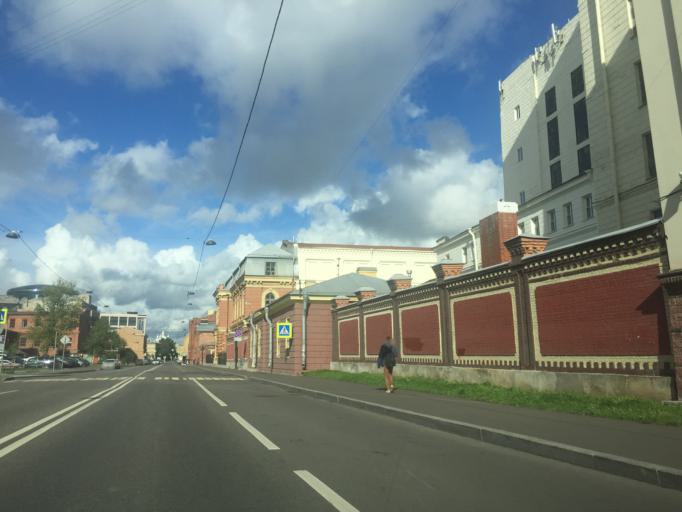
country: RU
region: St.-Petersburg
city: Centralniy
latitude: 59.9345
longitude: 30.3847
